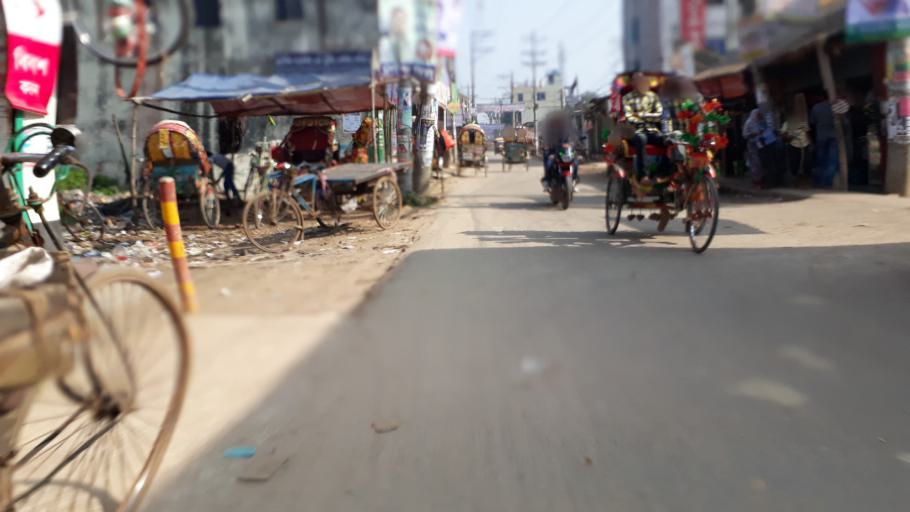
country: BD
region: Dhaka
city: Tungi
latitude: 23.8481
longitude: 90.2726
